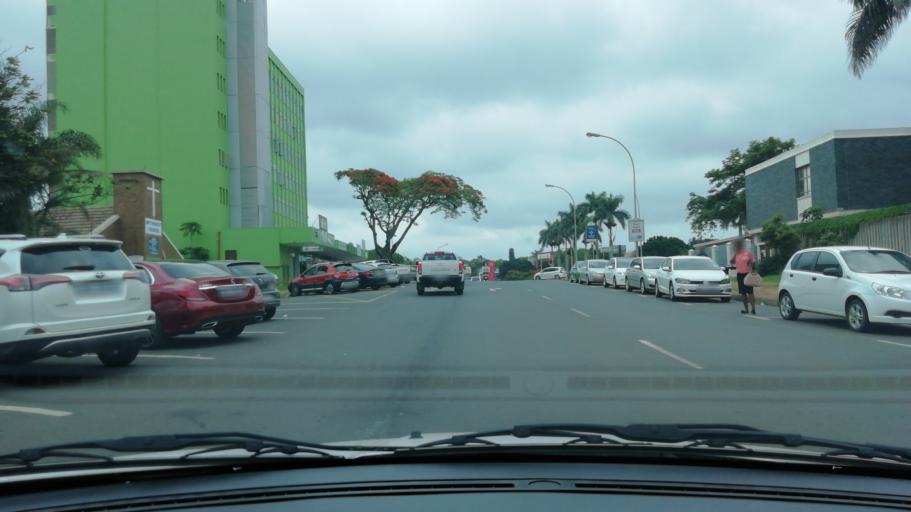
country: ZA
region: KwaZulu-Natal
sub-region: uThungulu District Municipality
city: Empangeni
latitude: -28.7444
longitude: 31.8922
